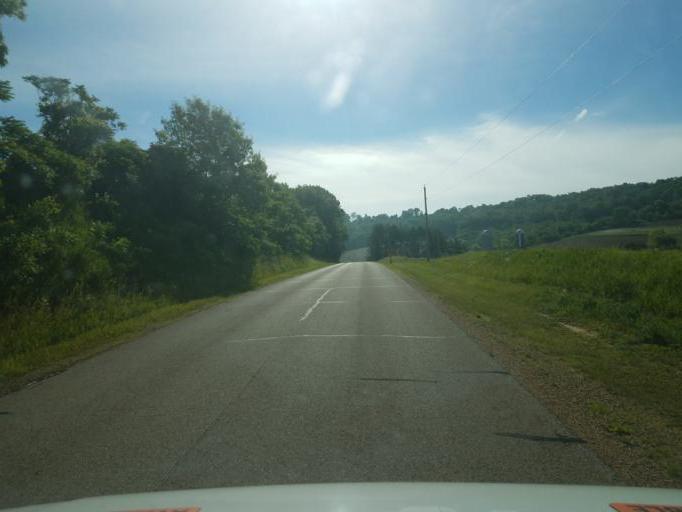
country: US
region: Wisconsin
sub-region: Sauk County
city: Reedsburg
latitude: 43.5478
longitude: -90.1177
